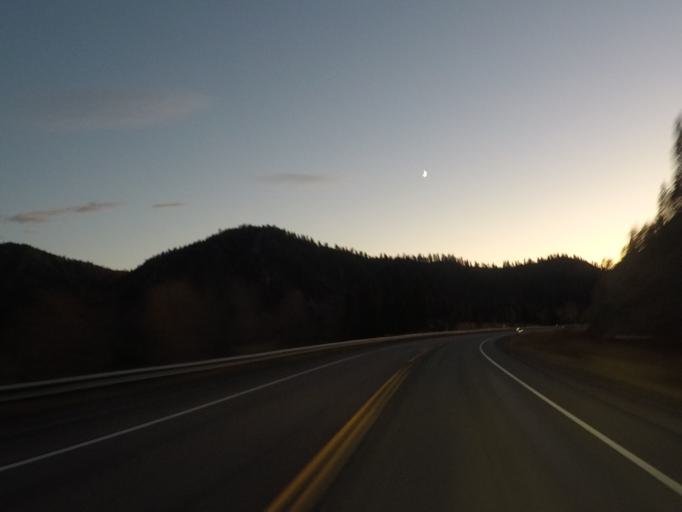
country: US
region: Montana
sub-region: Missoula County
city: Seeley Lake
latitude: 47.0238
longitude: -113.2902
